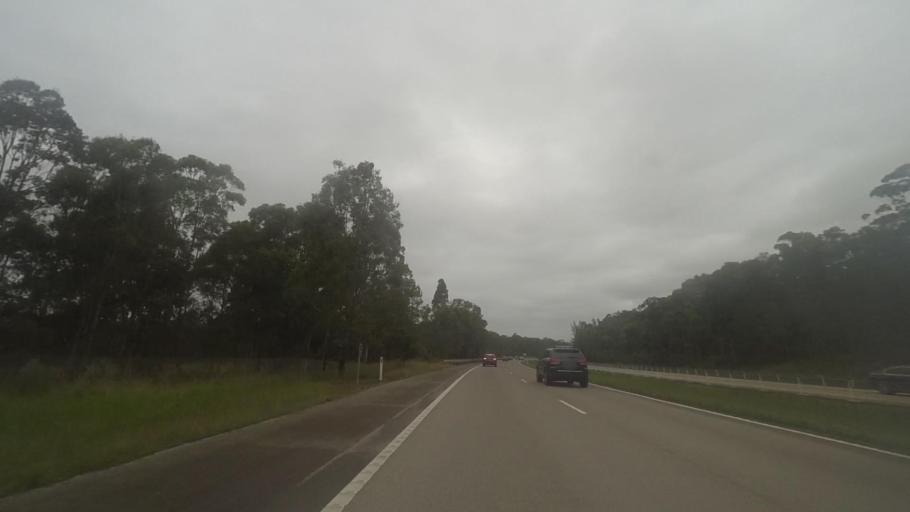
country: AU
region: New South Wales
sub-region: Port Stephens Shire
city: Medowie
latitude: -32.6926
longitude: 151.8088
